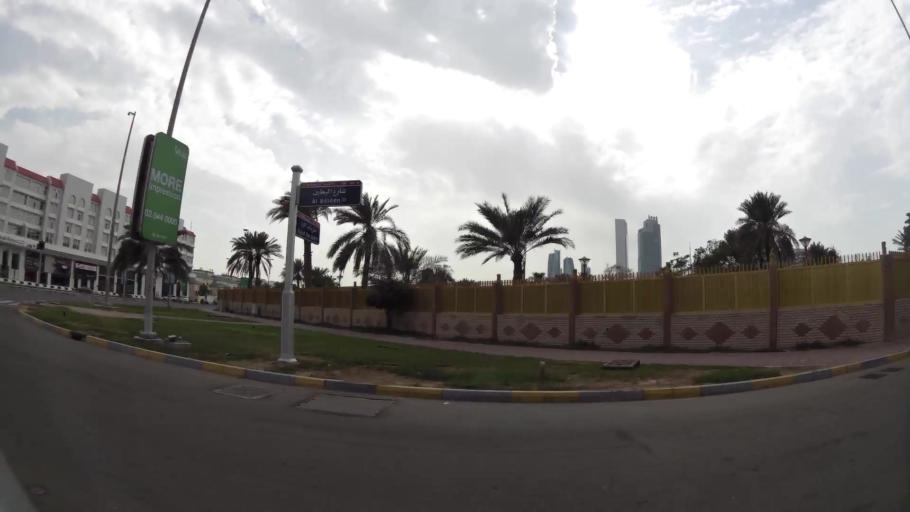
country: AE
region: Abu Dhabi
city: Abu Dhabi
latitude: 24.4673
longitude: 54.3393
